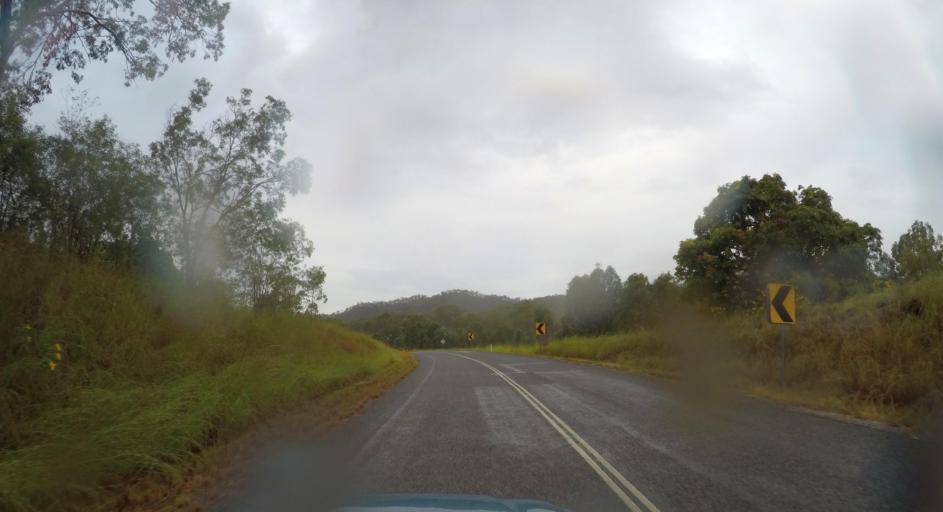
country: AU
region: Queensland
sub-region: Gladstone
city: Toolooa
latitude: -24.5458
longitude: 151.3656
